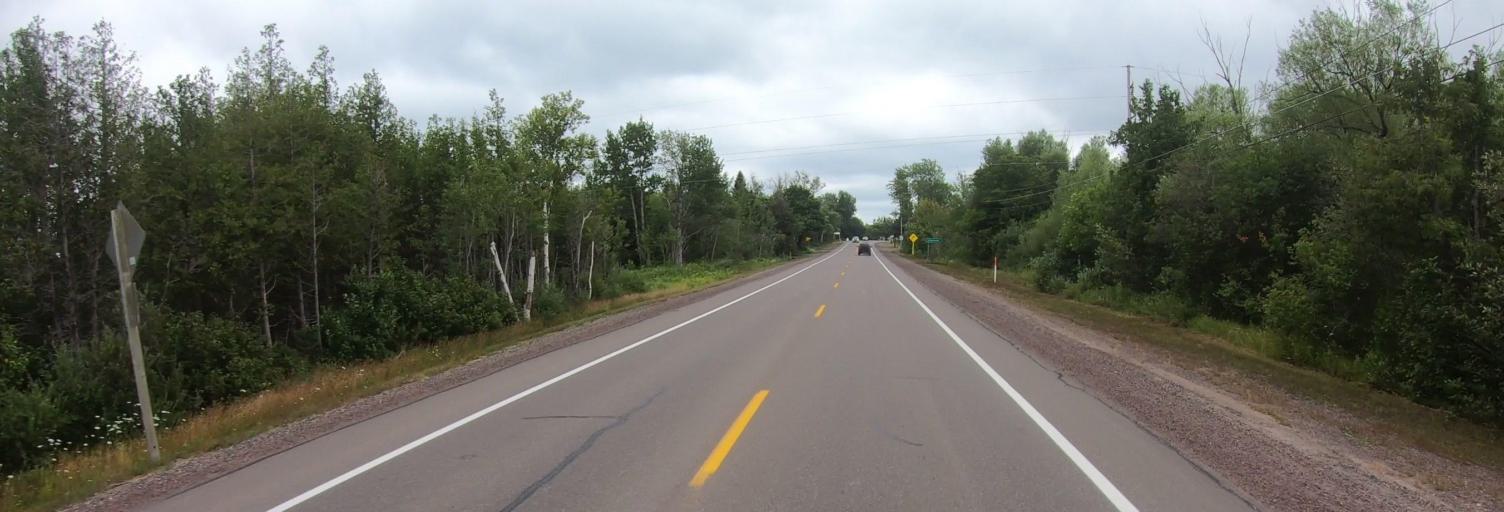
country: US
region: Michigan
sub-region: Houghton County
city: Laurium
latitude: 47.2629
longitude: -88.4255
